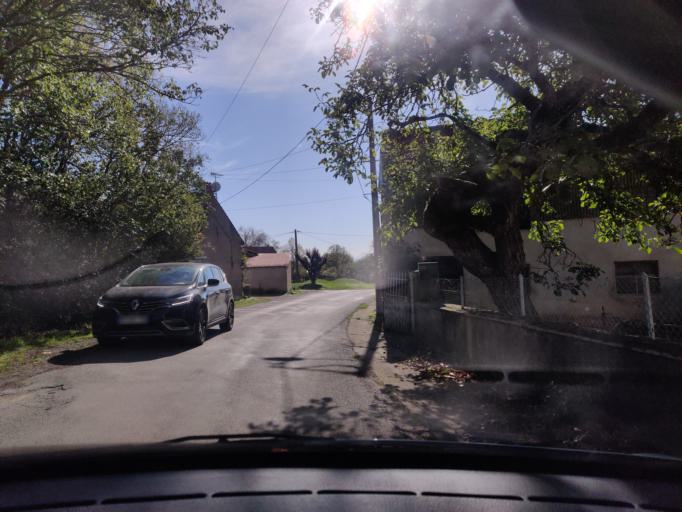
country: FR
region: Auvergne
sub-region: Departement du Puy-de-Dome
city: Combronde
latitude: 46.0221
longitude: 3.0973
